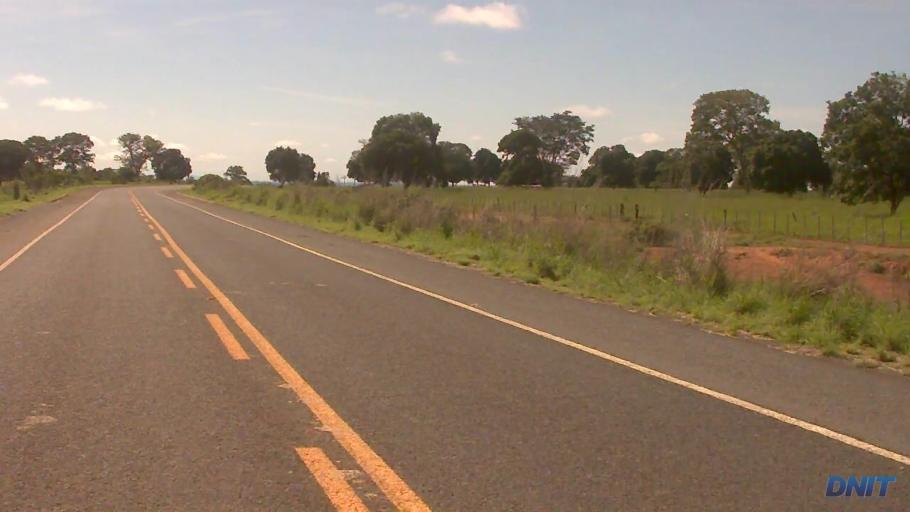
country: BR
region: Goias
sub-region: Sao Miguel Do Araguaia
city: Sao Miguel do Araguaia
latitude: -13.3186
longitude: -50.1627
